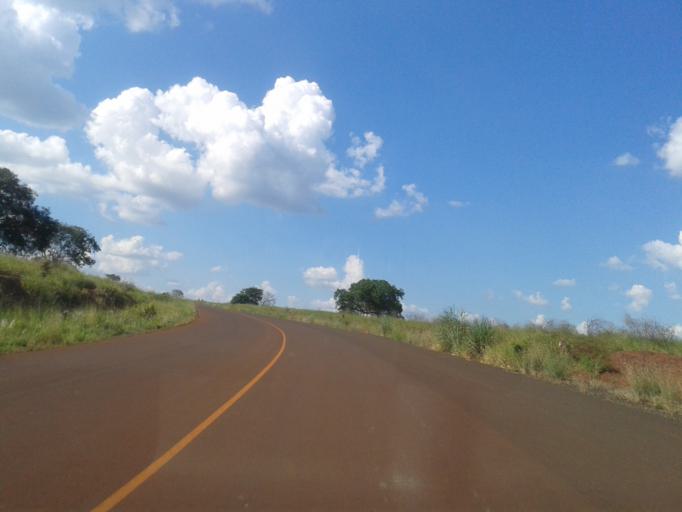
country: BR
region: Minas Gerais
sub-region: Ituiutaba
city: Ituiutaba
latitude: -19.1923
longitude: -49.5162
